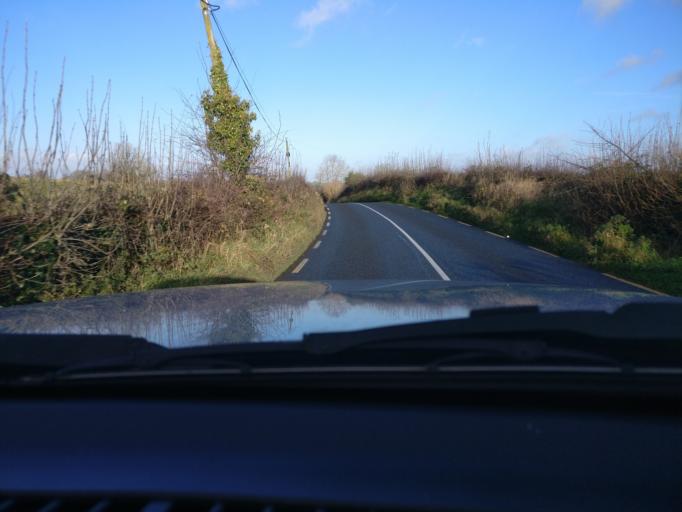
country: IE
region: Leinster
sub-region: An Iarmhi
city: Kilbeggan
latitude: 53.4649
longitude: -7.4941
